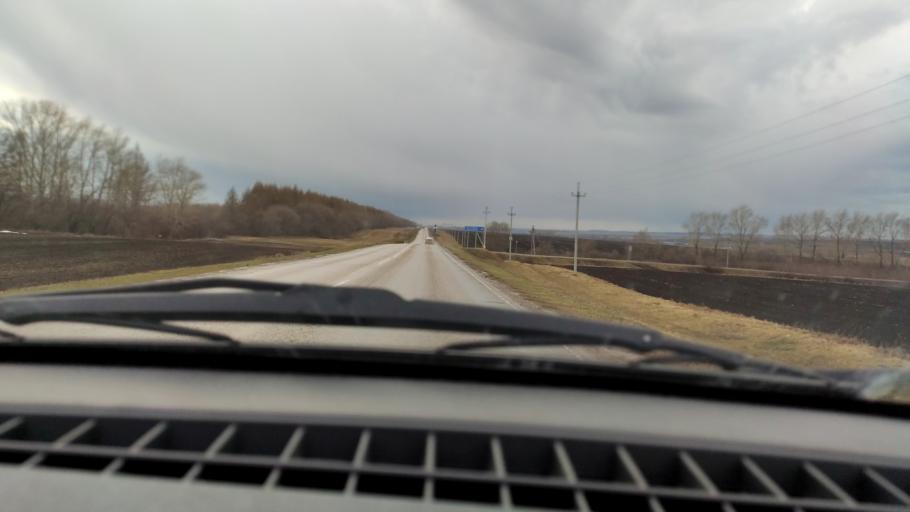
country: RU
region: Bashkortostan
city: Chekmagush
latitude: 55.1097
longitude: 54.9417
